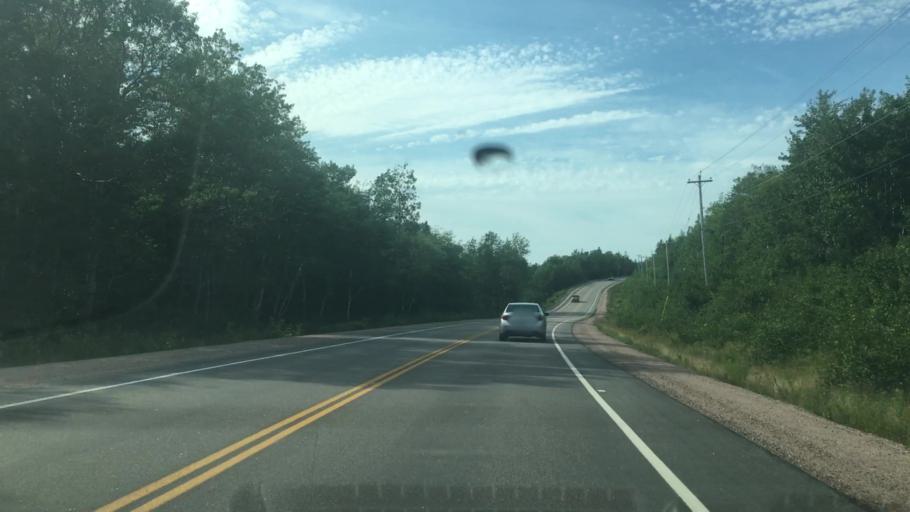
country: CA
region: Nova Scotia
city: Sydney Mines
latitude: 46.8206
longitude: -60.3543
